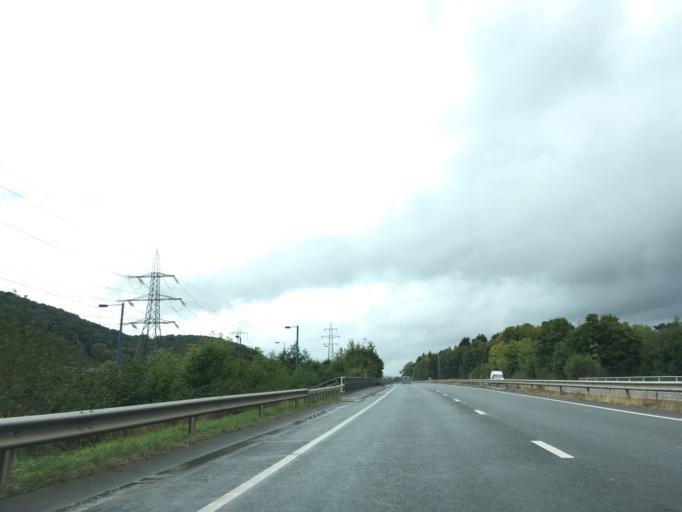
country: GB
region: Wales
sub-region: Monmouthshire
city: Abergavenny
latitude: 51.8152
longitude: -3.0269
